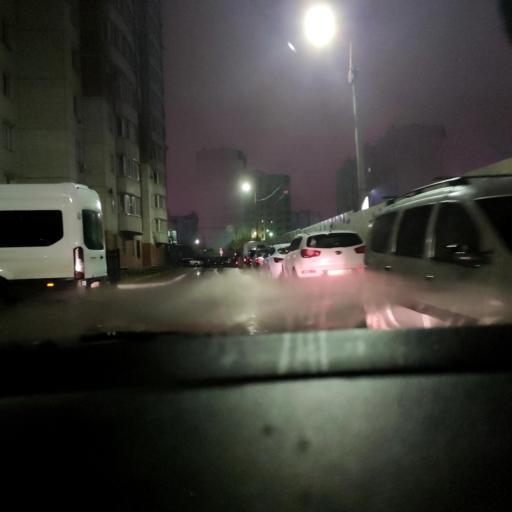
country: RU
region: Voronezj
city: Podgornoye
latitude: 51.7140
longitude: 39.1578
